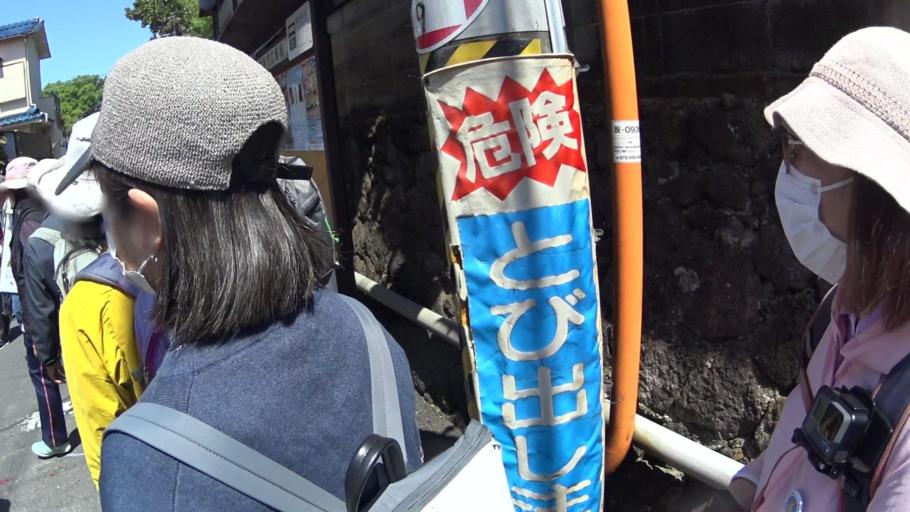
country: JP
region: Osaka
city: Kashihara
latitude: 34.5682
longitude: 135.6114
